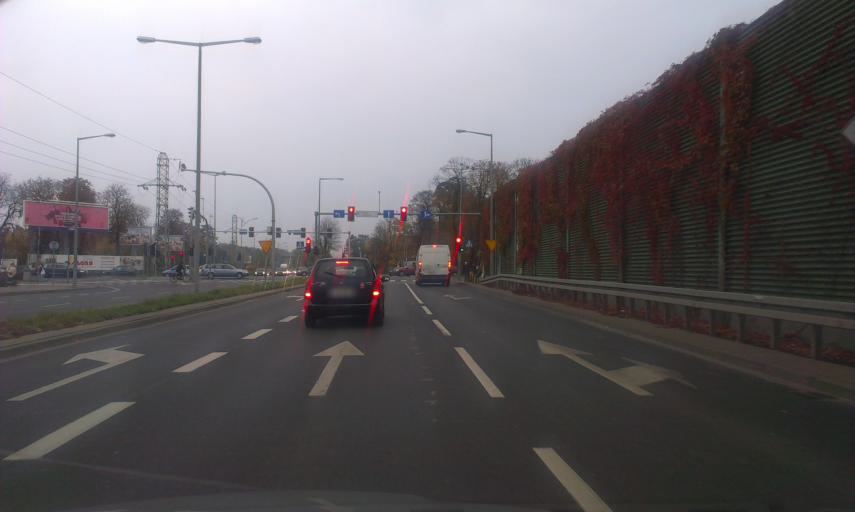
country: PL
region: Greater Poland Voivodeship
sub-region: Poznan
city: Poznan
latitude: 52.4114
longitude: 16.8693
